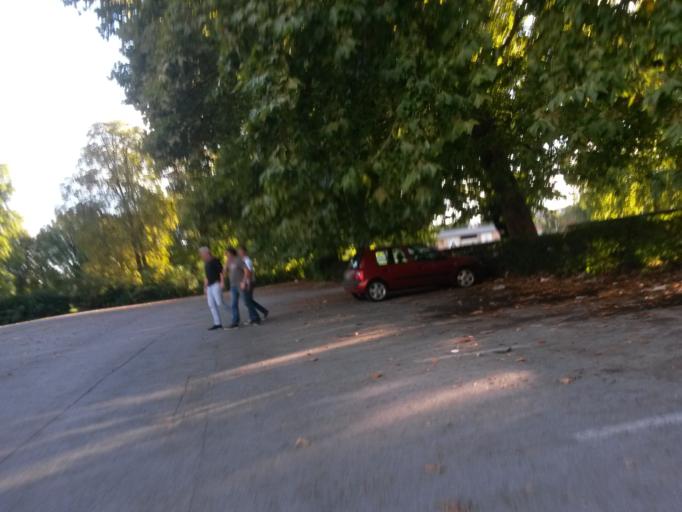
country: HR
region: Osjecko-Baranjska
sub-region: Grad Osijek
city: Osijek
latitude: 45.5559
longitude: 18.7122
